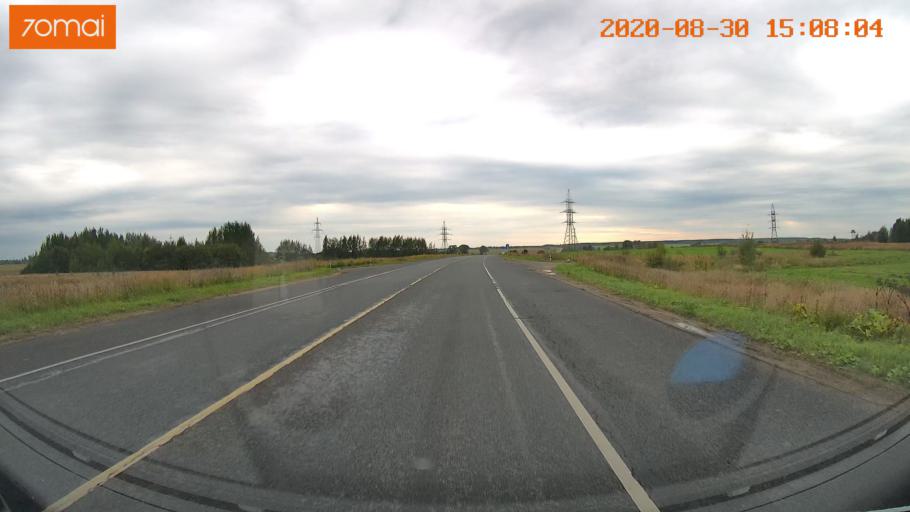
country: RU
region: Ivanovo
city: Staraya Vichuga
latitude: 57.2436
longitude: 41.8921
